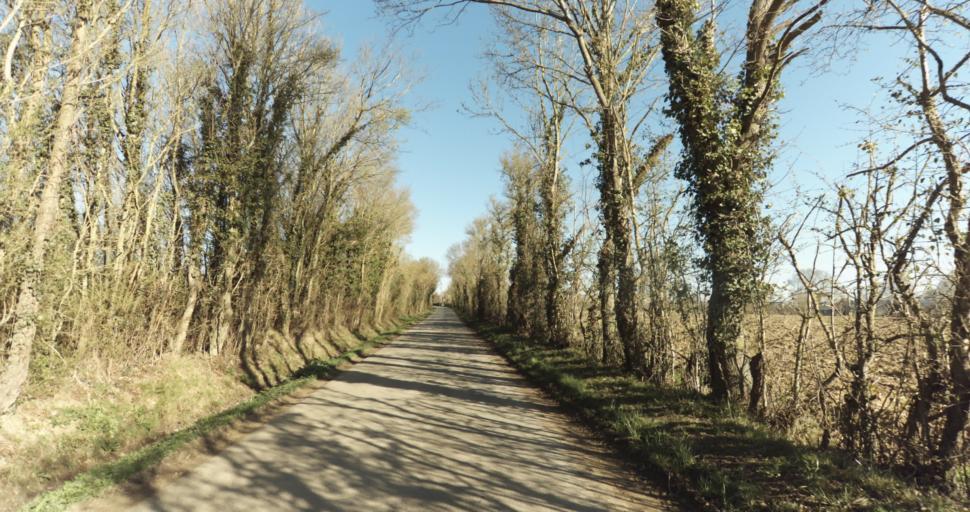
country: FR
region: Lower Normandy
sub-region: Departement du Calvados
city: Saint-Pierre-sur-Dives
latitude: 48.9953
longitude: -0.0026
